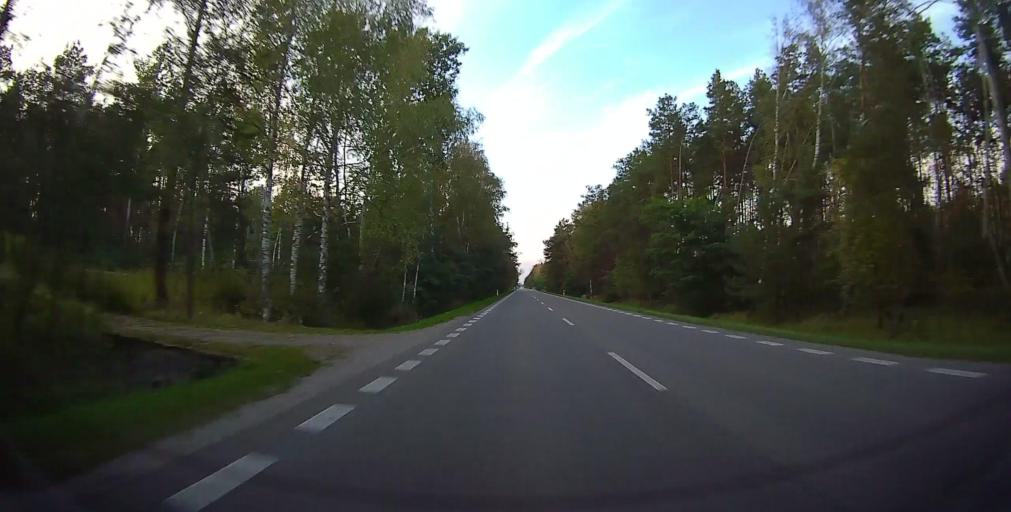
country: PL
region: Masovian Voivodeship
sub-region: Powiat kozienicki
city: Ryczywol
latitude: 51.6717
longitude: 21.4396
